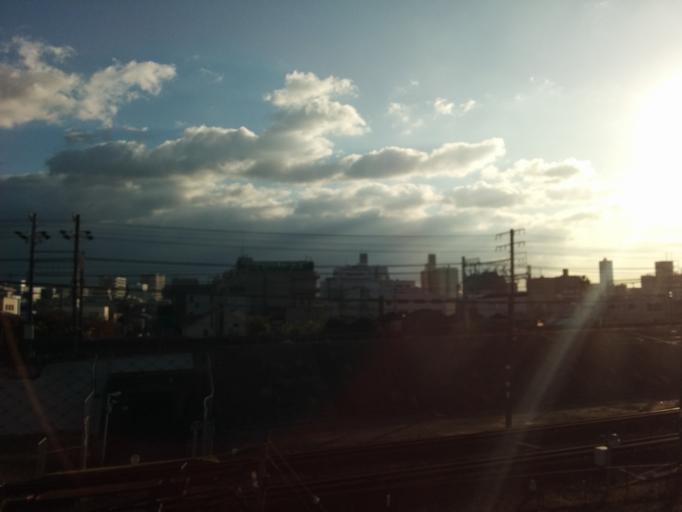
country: JP
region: Aichi
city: Nagoya-shi
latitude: 35.1506
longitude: 136.8881
